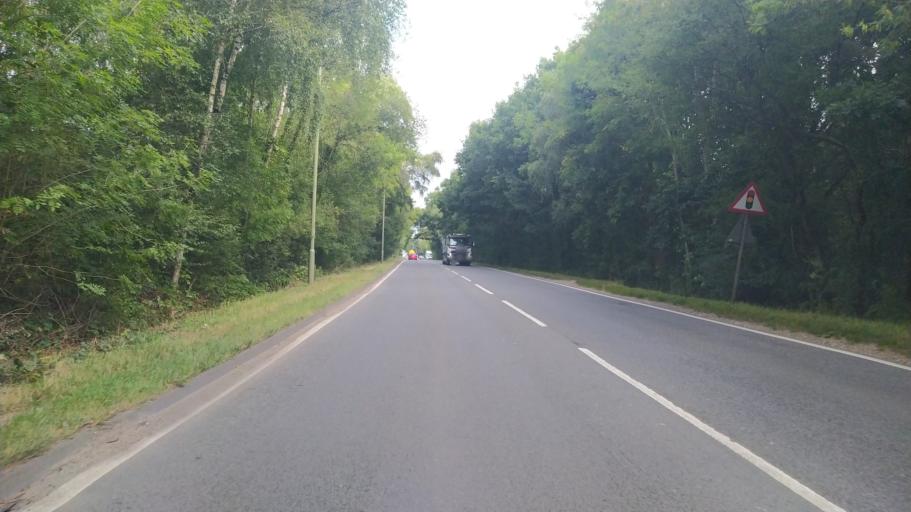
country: GB
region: England
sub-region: Hampshire
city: Totton
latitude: 50.9084
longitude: -1.4879
